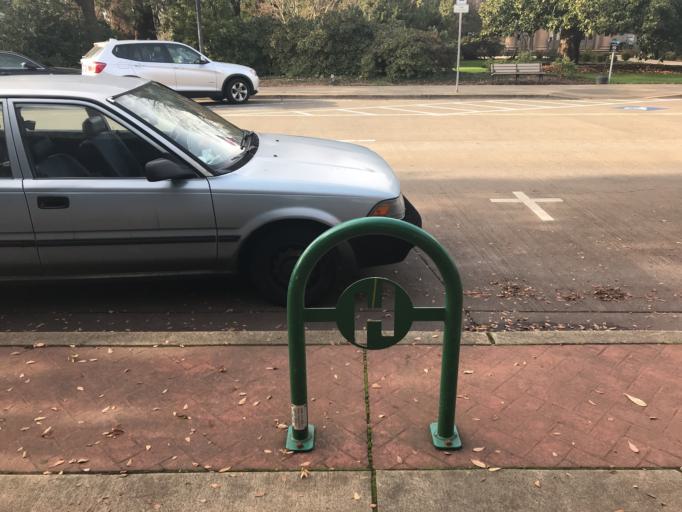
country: US
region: Oregon
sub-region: Washington County
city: Hillsboro
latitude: 45.5231
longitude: -122.9879
